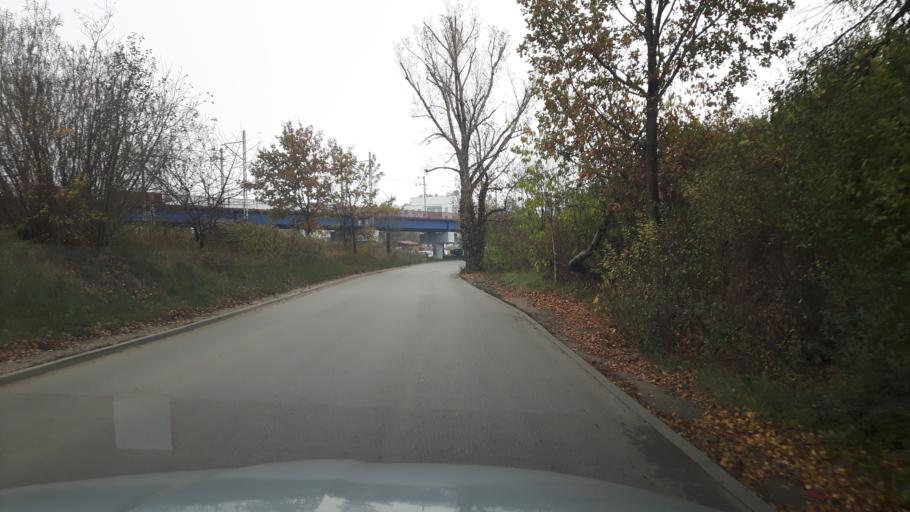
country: PL
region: Masovian Voivodeship
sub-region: Warszawa
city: Wlochy
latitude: 52.2032
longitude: 20.9434
